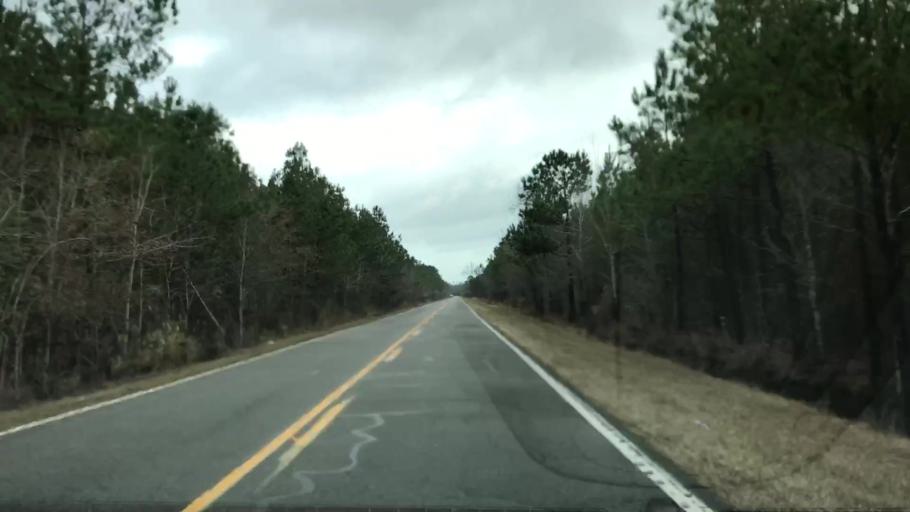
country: US
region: South Carolina
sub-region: Georgetown County
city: Murrells Inlet
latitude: 33.6254
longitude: -79.2398
